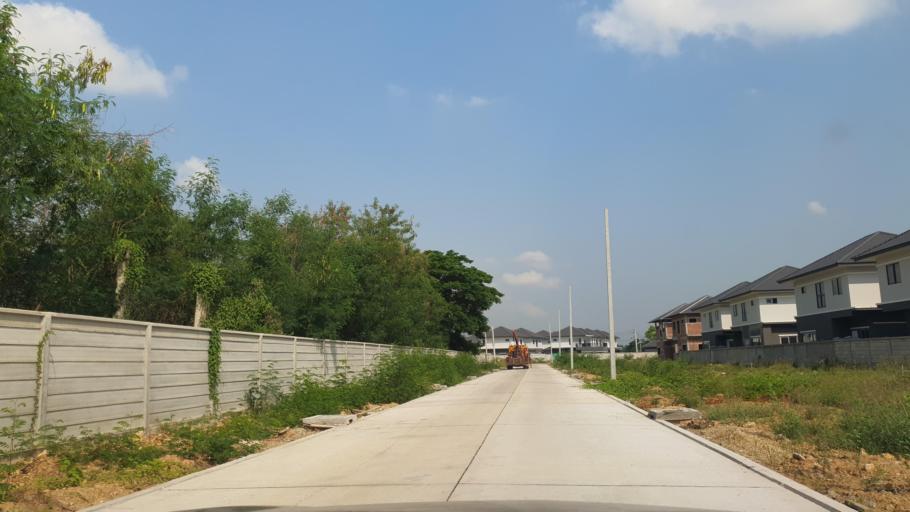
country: TH
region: Chiang Mai
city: San Kamphaeng
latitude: 18.7631
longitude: 99.0964
